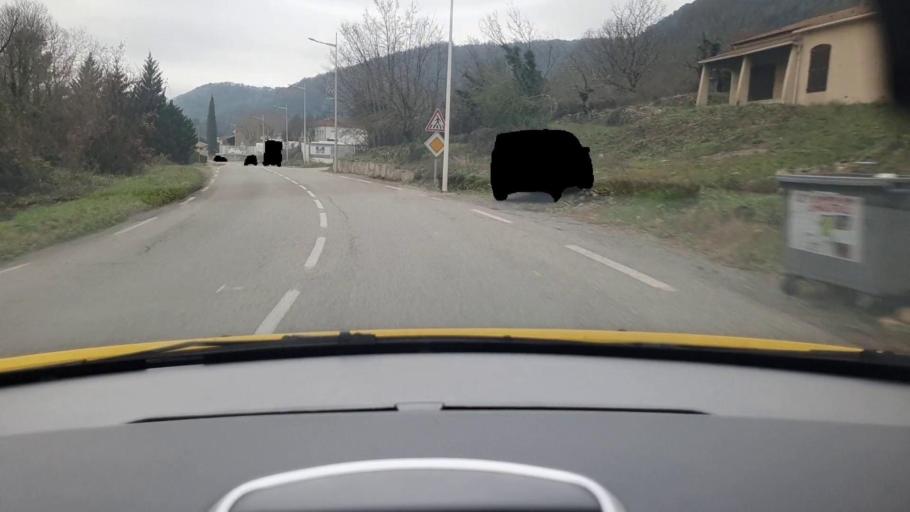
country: FR
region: Languedoc-Roussillon
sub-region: Departement du Gard
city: Molieres-sur-Ceze
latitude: 44.2762
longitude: 4.1502
